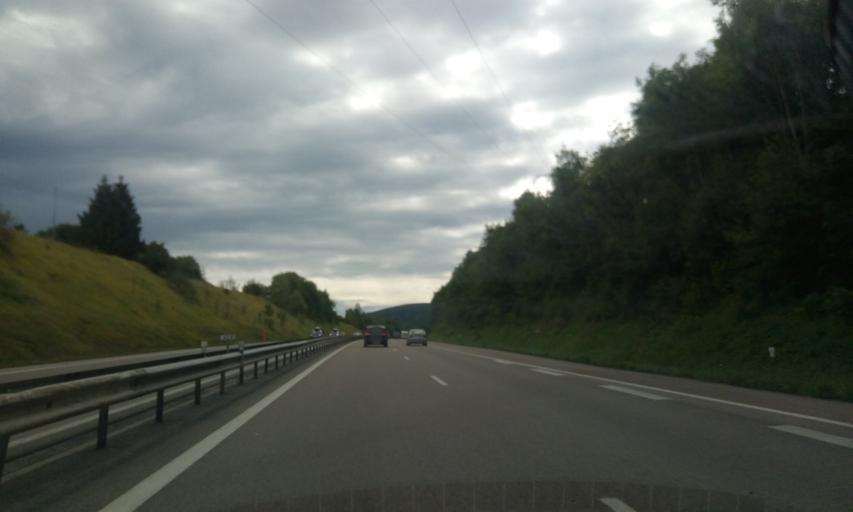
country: FR
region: Rhone-Alpes
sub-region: Departement de l'Isere
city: Chabons
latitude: 45.4248
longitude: 5.4405
